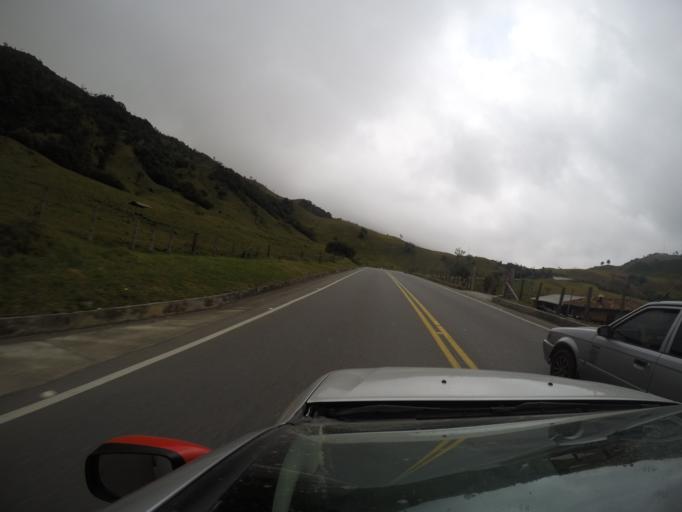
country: CO
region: Tolima
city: Herveo
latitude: 5.0334
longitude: -75.3336
